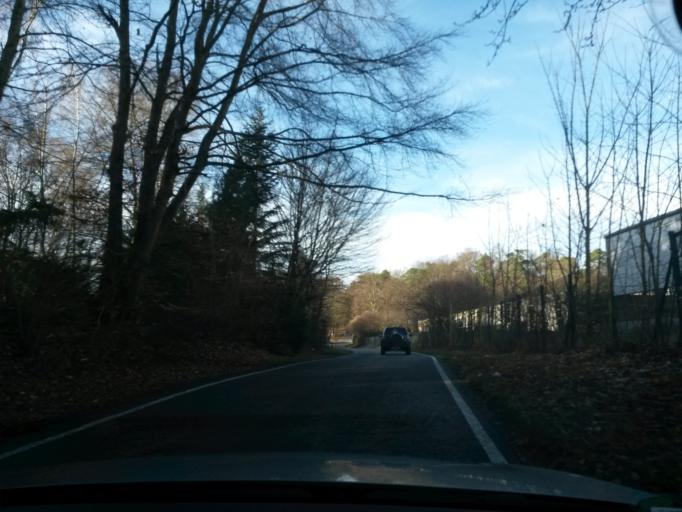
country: DE
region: Baden-Wuerttemberg
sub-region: Karlsruhe Region
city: Ispringen
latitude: 48.8987
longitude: 8.6555
